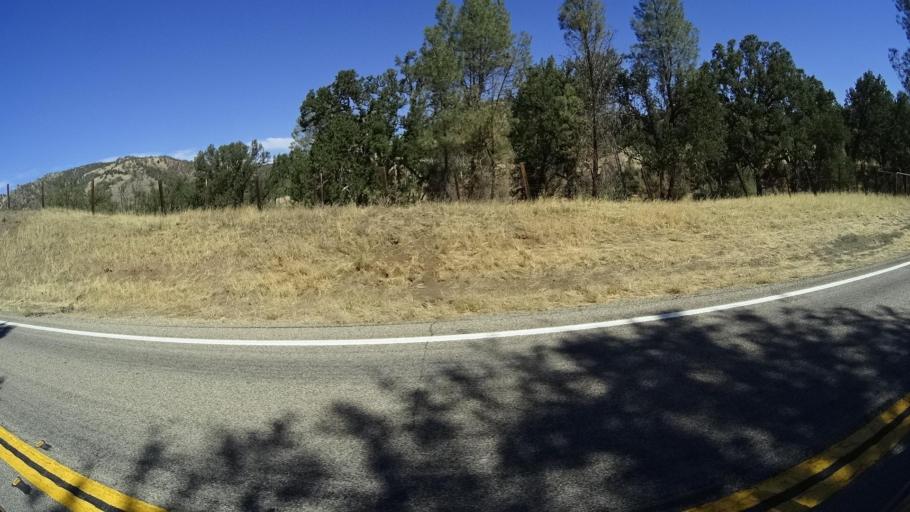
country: US
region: California
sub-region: Fresno County
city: Coalinga
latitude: 36.2002
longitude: -120.7295
